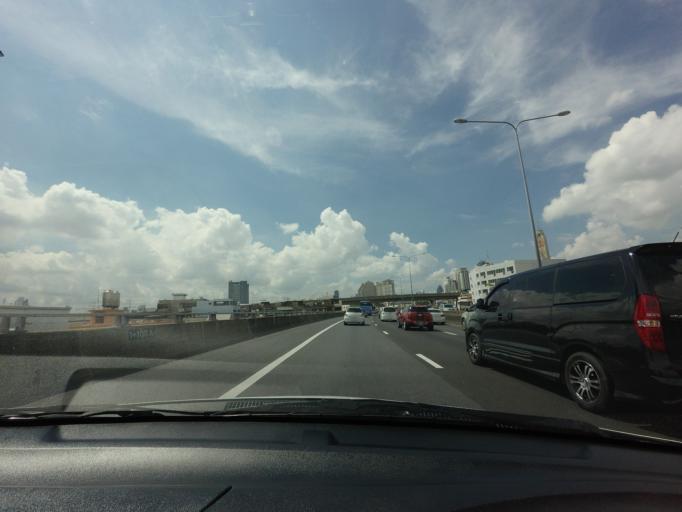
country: TH
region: Bangkok
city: Ratchathewi
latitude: 13.7680
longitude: 100.5384
